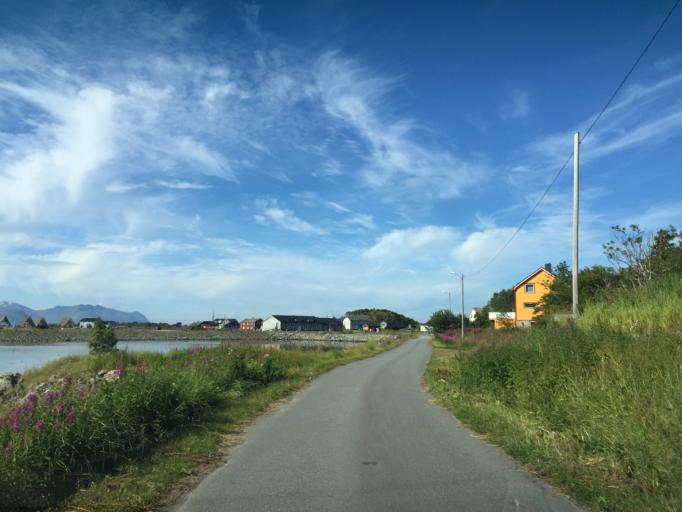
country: NO
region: Nordland
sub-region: Vagan
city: Kabelvag
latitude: 68.3872
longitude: 14.4240
